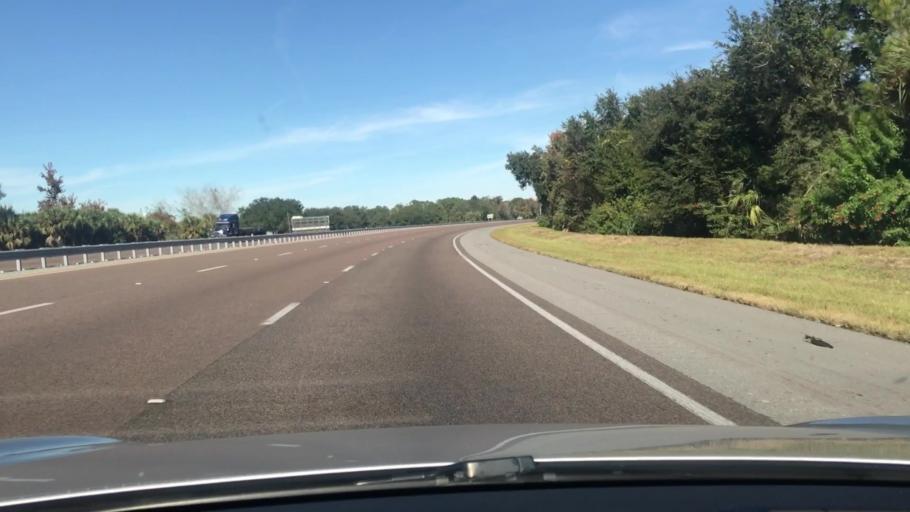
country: US
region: Florida
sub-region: Brevard County
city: Mims
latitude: 28.7183
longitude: -80.8903
